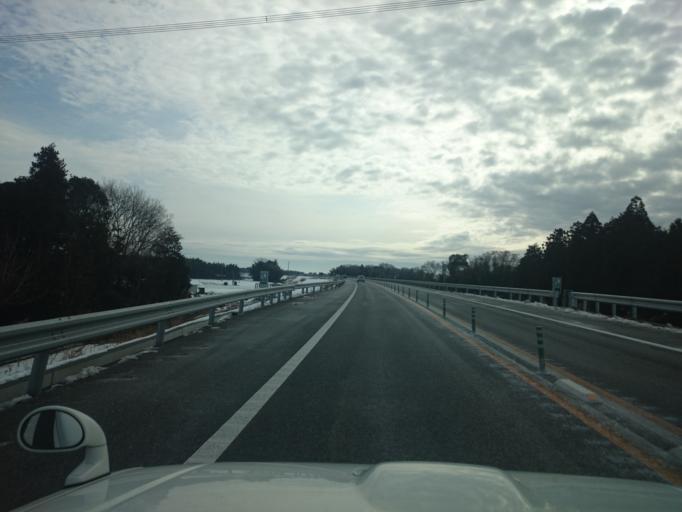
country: JP
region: Ibaraki
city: Sakai
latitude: 36.1157
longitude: 139.8382
